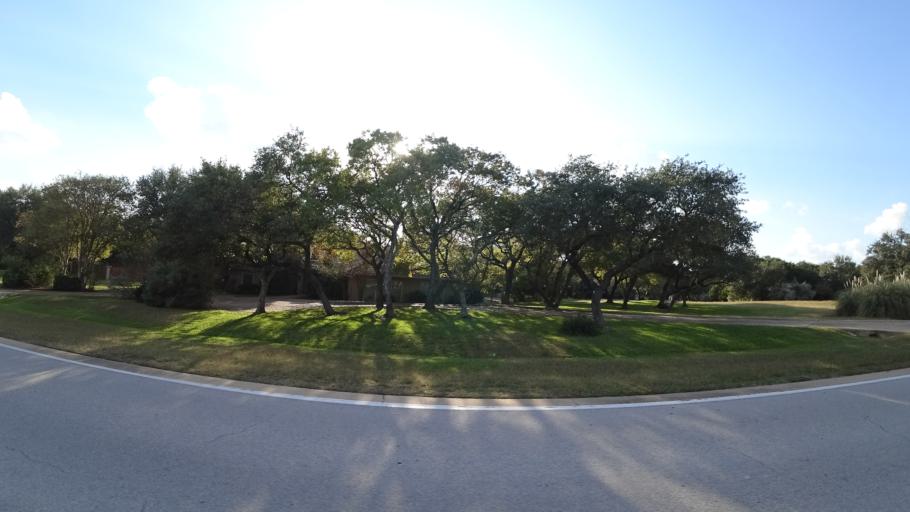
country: US
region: Texas
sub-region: Travis County
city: Barton Creek
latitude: 30.2805
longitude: -97.8712
